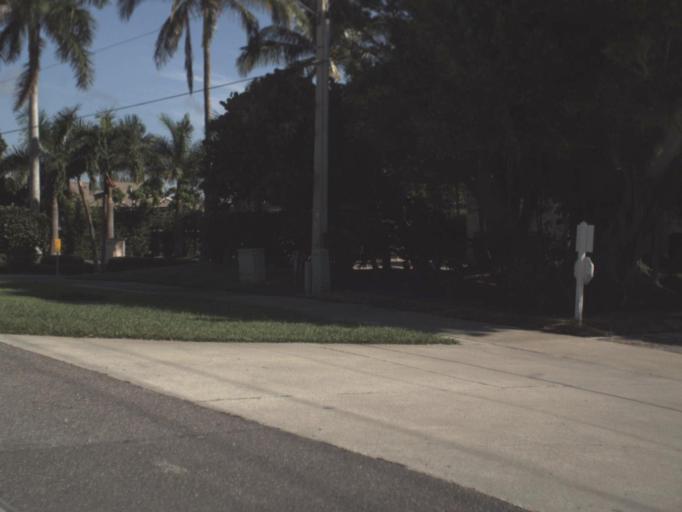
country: US
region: Florida
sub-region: Manatee County
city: Longboat Key
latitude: 27.3896
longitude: -82.6411
